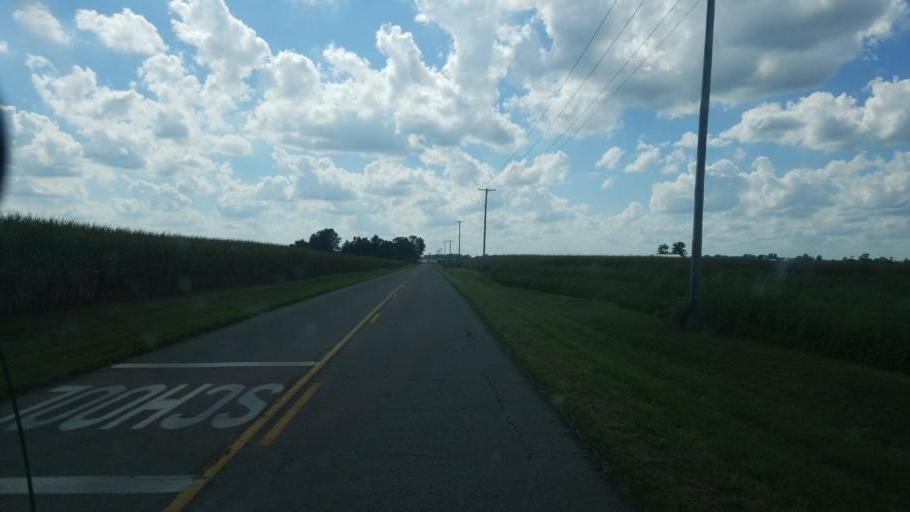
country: US
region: Ohio
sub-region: Union County
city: Richwood
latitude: 40.4377
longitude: -83.3069
